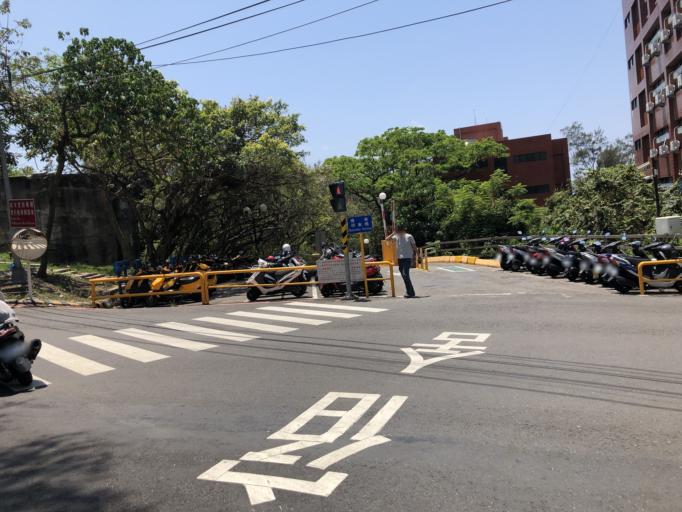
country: TW
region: Kaohsiung
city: Kaohsiung
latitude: 22.6277
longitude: 120.2691
